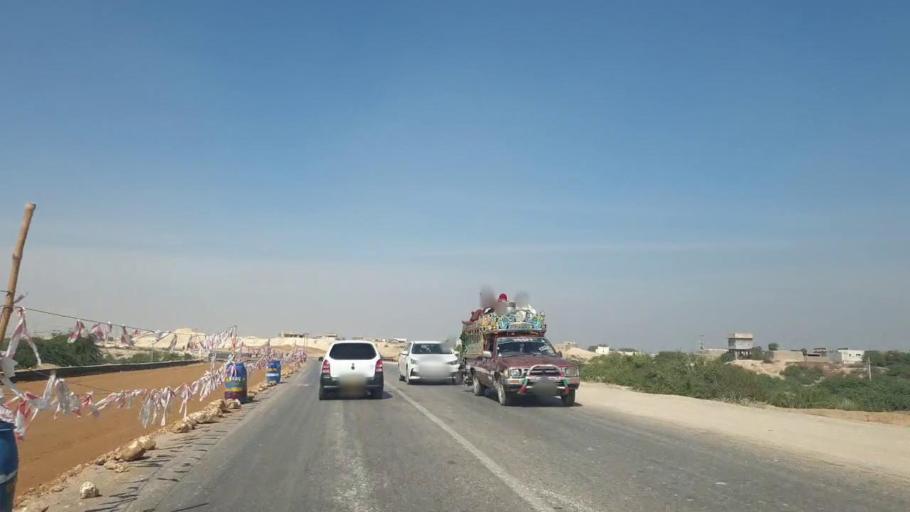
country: PK
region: Sindh
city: Hala
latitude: 25.7315
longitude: 68.2928
